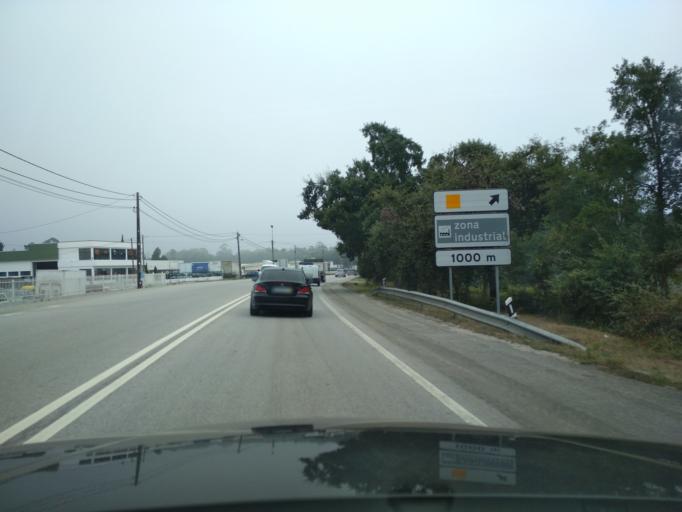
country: PT
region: Aveiro
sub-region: Mealhada
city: Pampilhosa do Botao
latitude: 40.3383
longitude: -8.4518
